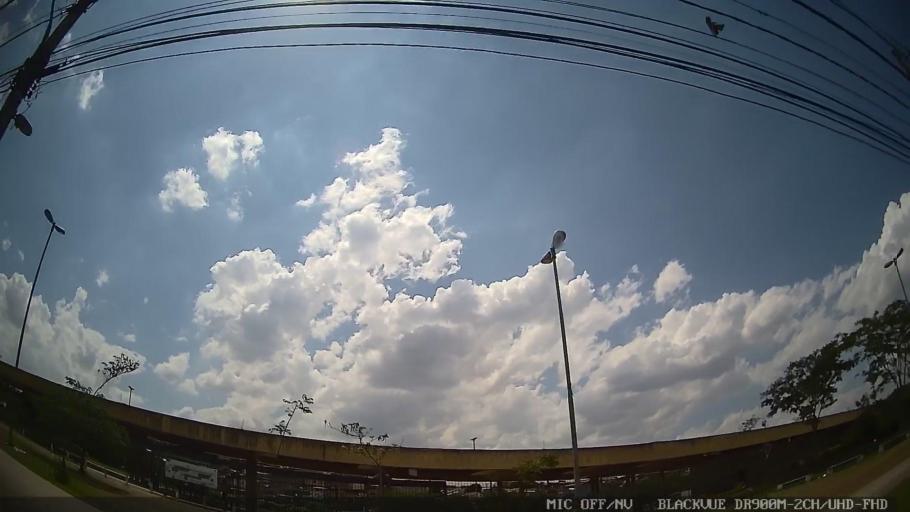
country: BR
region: Sao Paulo
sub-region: Ferraz De Vasconcelos
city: Ferraz de Vasconcelos
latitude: -23.5431
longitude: -46.4597
